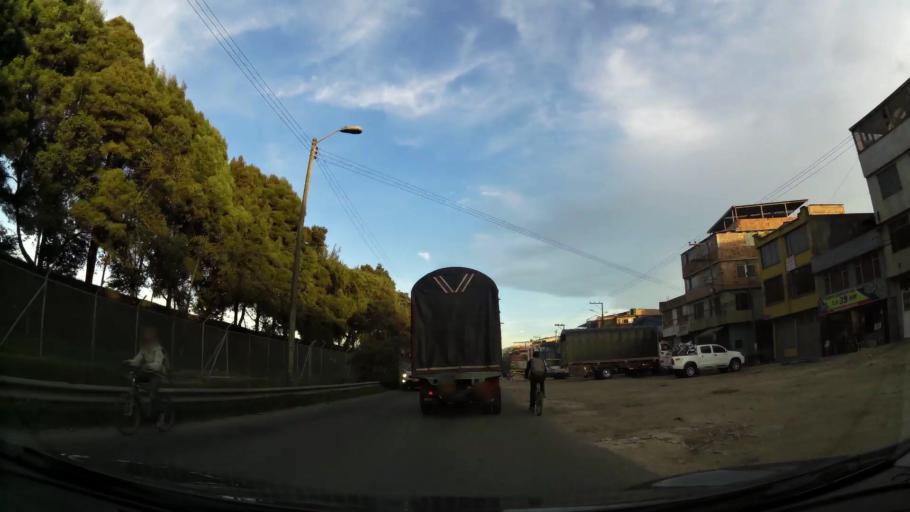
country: CO
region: Cundinamarca
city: Funza
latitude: 4.6929
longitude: -74.1489
